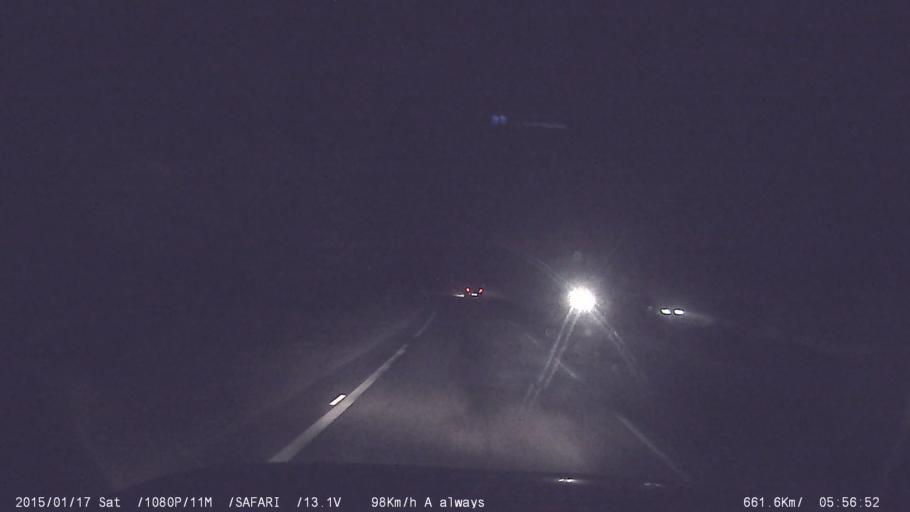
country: IN
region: Tamil Nadu
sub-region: Vellore
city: Walajapet
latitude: 12.8984
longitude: 79.5324
